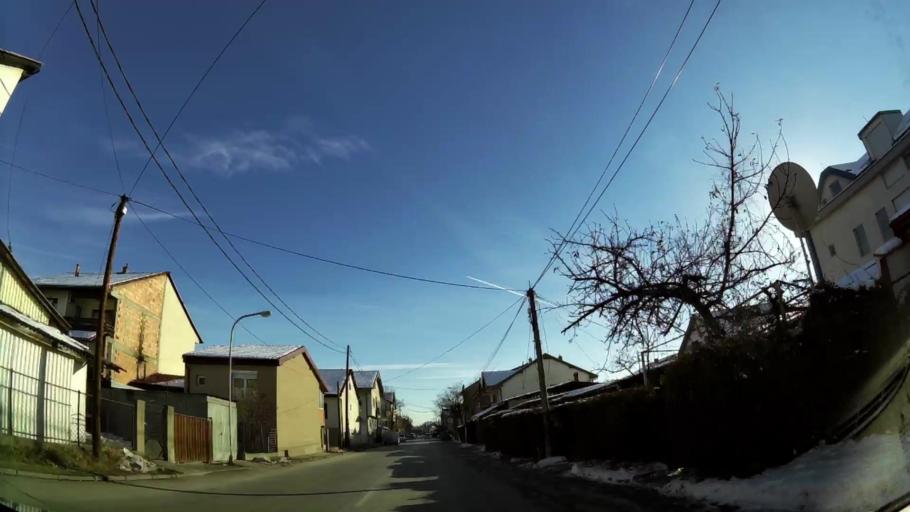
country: MK
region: Saraj
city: Saraj
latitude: 42.0084
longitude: 21.3408
